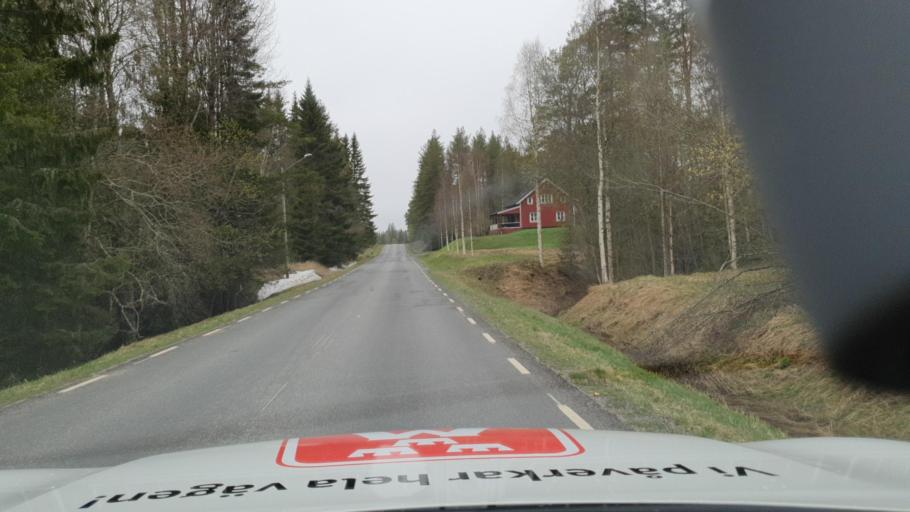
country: SE
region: Vaesterbotten
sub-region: Nordmalings Kommun
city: Nordmaling
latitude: 63.7105
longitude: 19.5825
